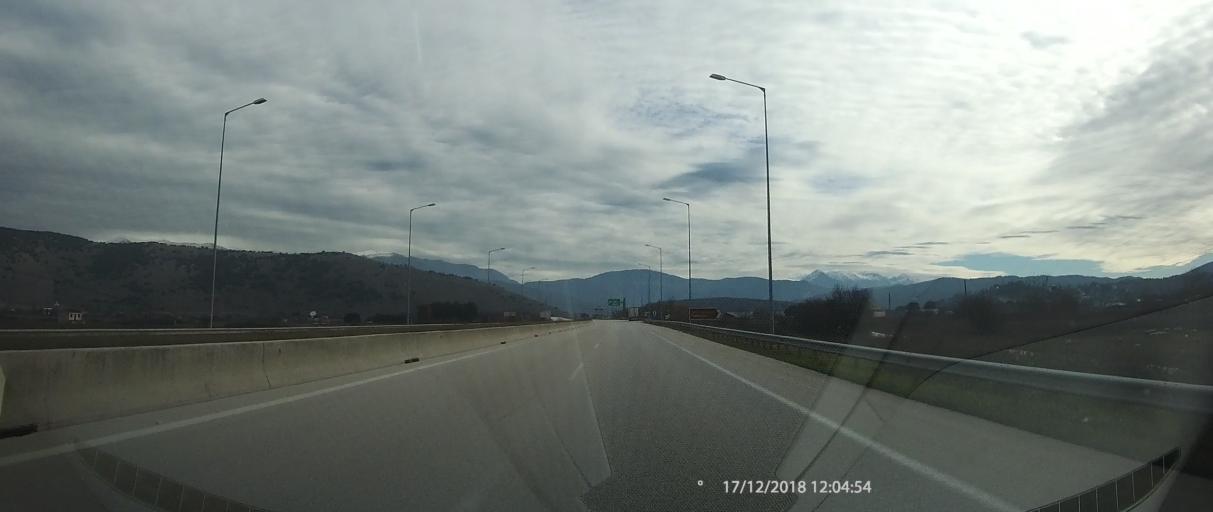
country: GR
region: Epirus
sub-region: Nomos Ioanninon
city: Koutselio
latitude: 39.6014
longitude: 20.8967
